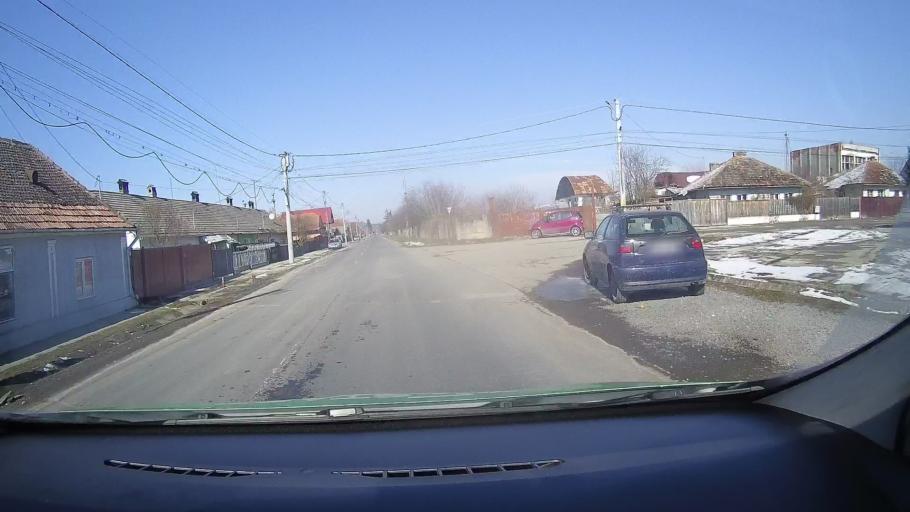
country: RO
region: Brasov
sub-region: Comuna Homorod
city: Homorod
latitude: 46.0176
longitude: 25.2751
